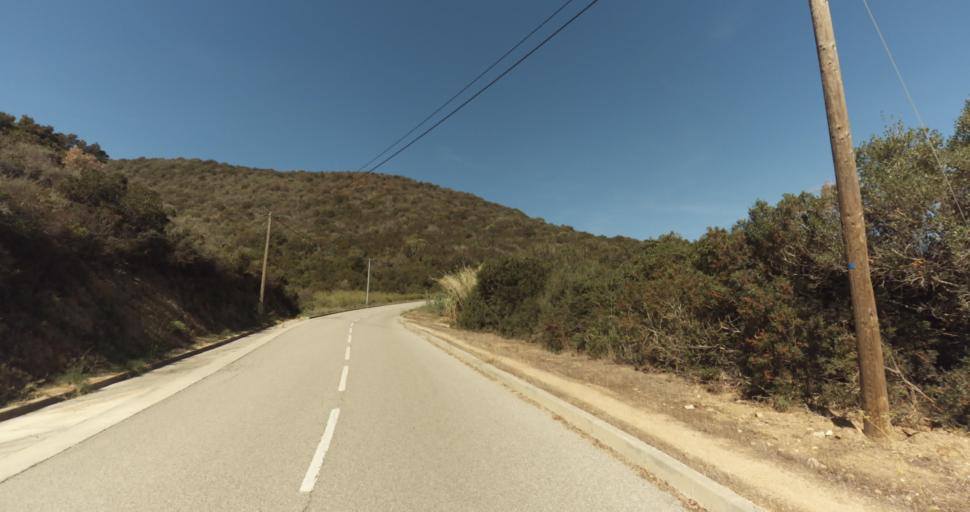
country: FR
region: Corsica
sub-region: Departement de la Corse-du-Sud
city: Ajaccio
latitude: 41.9202
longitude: 8.6431
